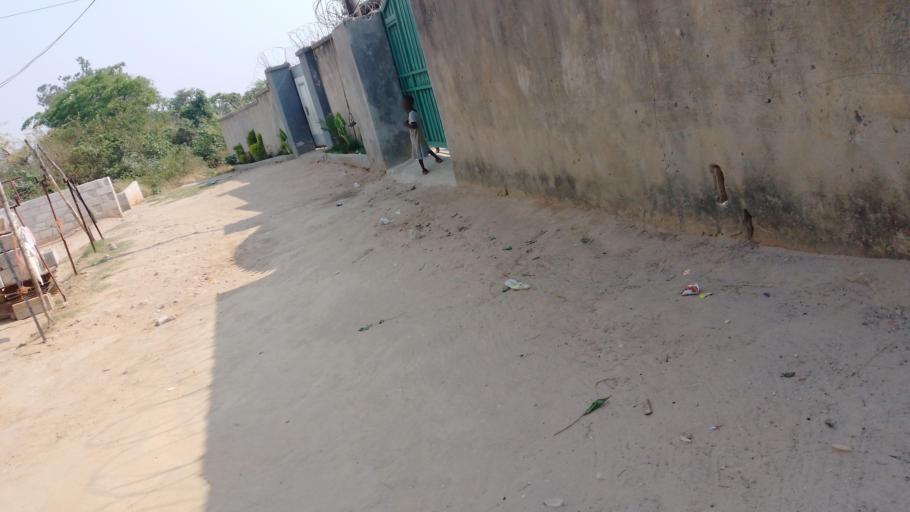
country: ZM
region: Lusaka
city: Lusaka
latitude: -15.4023
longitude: 28.3829
